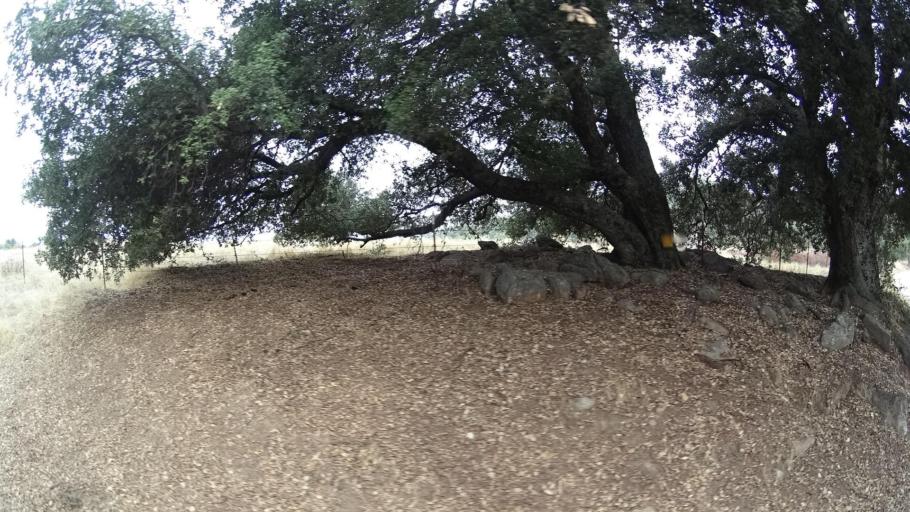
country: US
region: California
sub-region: San Diego County
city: Julian
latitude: 33.0435
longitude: -116.6423
